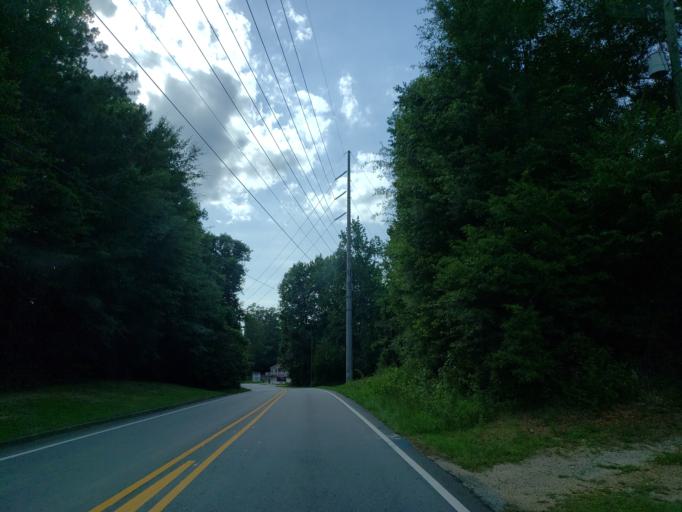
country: US
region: Georgia
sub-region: Cobb County
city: Powder Springs
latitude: 33.8731
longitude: -84.6387
